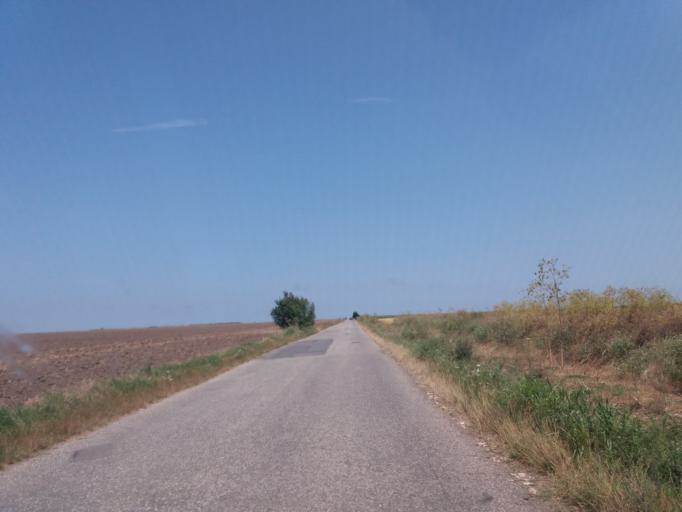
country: RO
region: Constanta
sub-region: Comuna Corbu
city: Corbu
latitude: 44.4240
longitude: 28.6725
